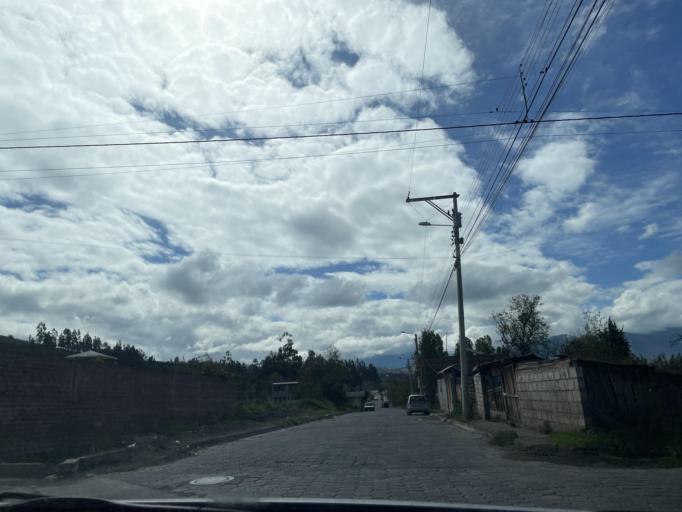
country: EC
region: Chimborazo
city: Guano
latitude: -1.6069
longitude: -78.6254
